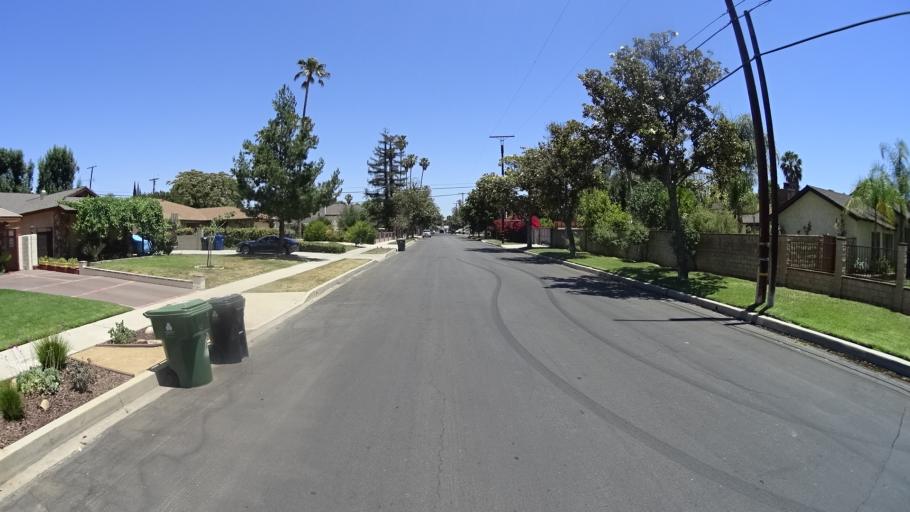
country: US
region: California
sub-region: Los Angeles County
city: Northridge
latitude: 34.1975
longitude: -118.5084
